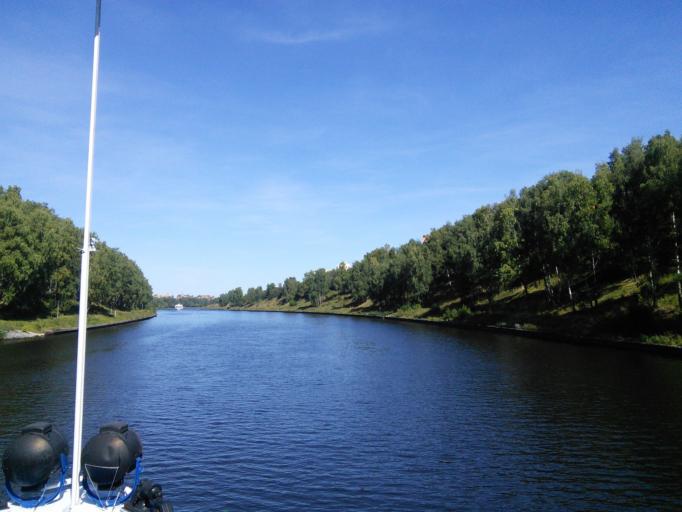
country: RU
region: Moskovskaya
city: Dolgoprudnyy
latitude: 55.9318
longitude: 37.4885
